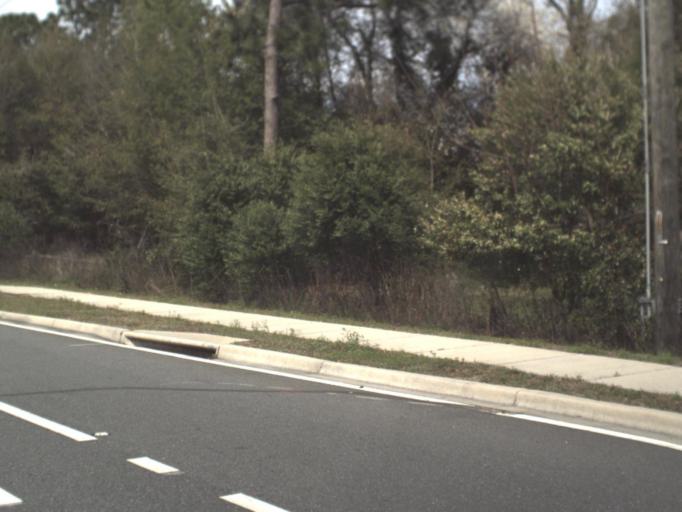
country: US
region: Florida
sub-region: Leon County
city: Tallahassee
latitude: 30.3759
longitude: -84.2688
